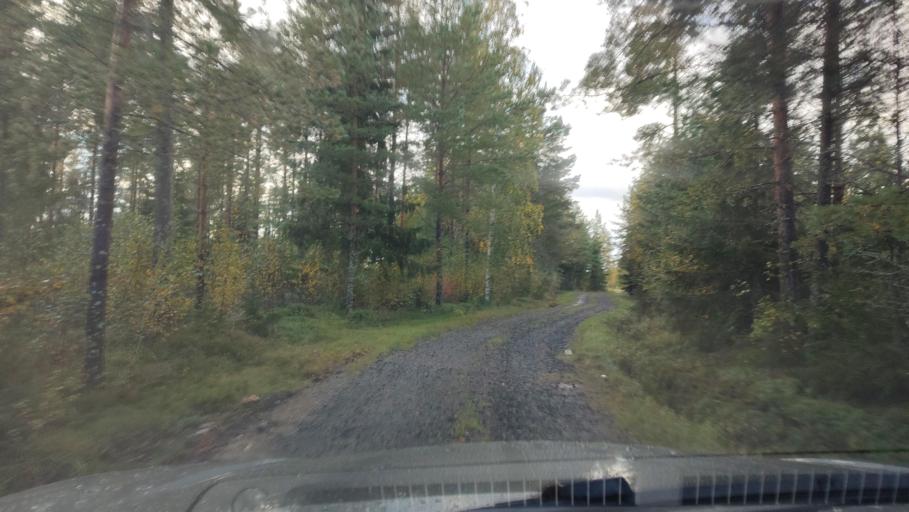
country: FI
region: Ostrobothnia
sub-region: Sydosterbotten
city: Kristinestad
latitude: 62.3017
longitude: 21.5080
